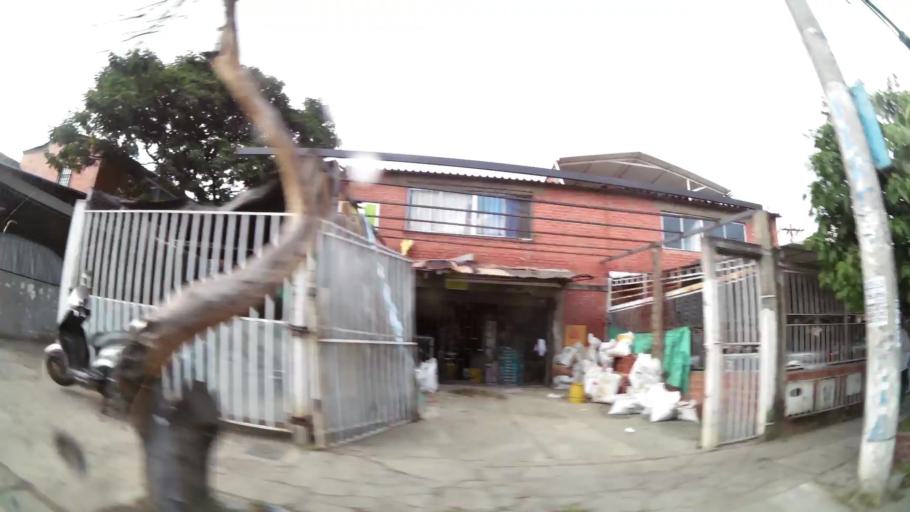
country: CO
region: Valle del Cauca
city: Cali
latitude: 3.4664
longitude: -76.4892
